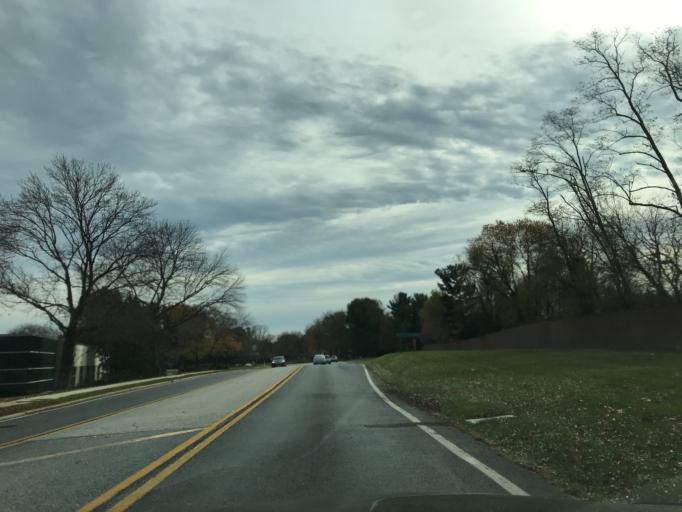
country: US
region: Maryland
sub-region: Howard County
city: Columbia
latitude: 39.2294
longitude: -76.8280
